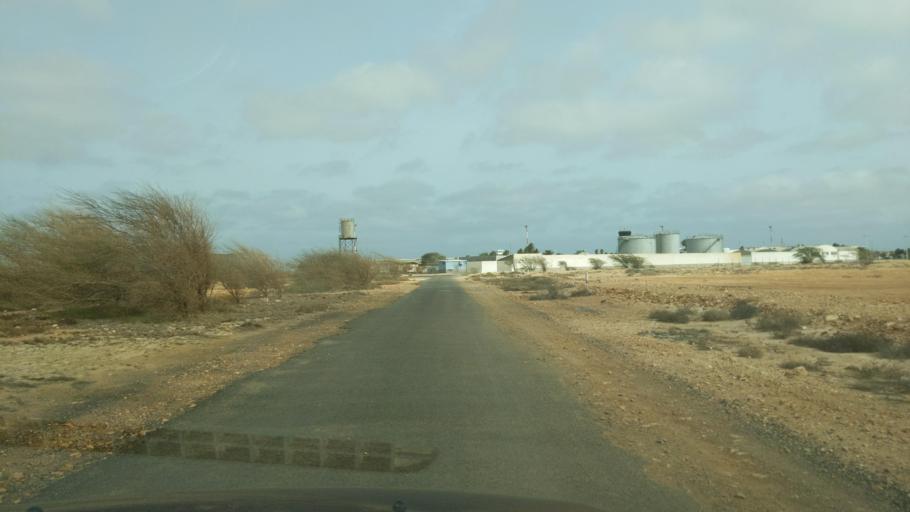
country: CV
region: Sal
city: Espargos
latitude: 16.7302
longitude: -22.9404
